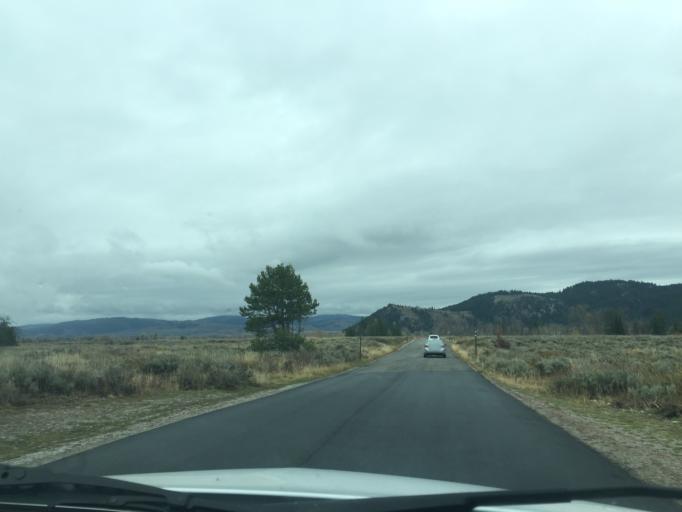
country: US
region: Wyoming
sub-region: Teton County
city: Moose Wilson Road
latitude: 43.6600
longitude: -110.7289
